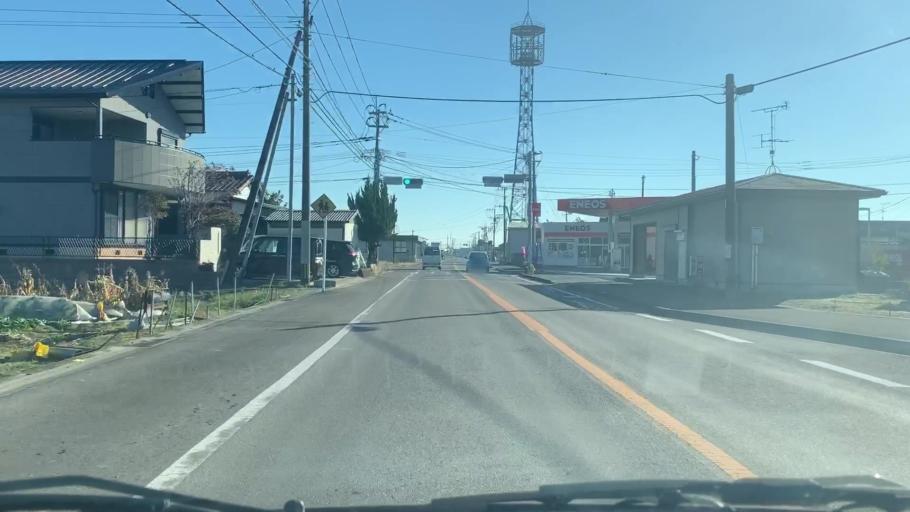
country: JP
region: Saga Prefecture
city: Kashima
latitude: 33.1826
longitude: 130.1813
